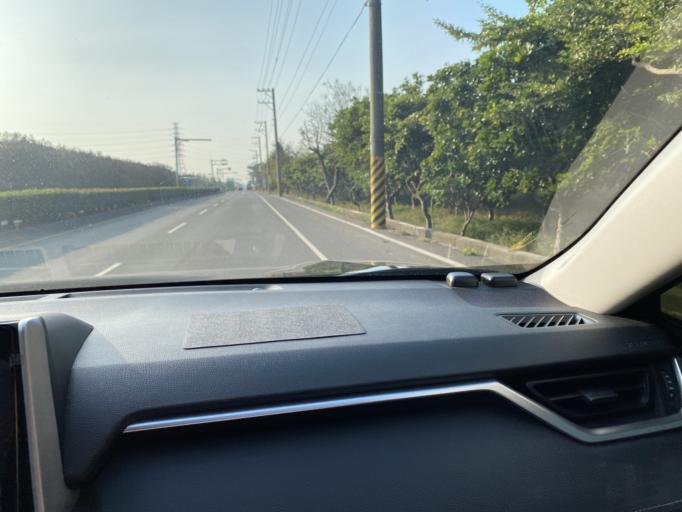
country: TW
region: Taiwan
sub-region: Changhua
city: Chang-hua
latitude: 23.9576
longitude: 120.4068
